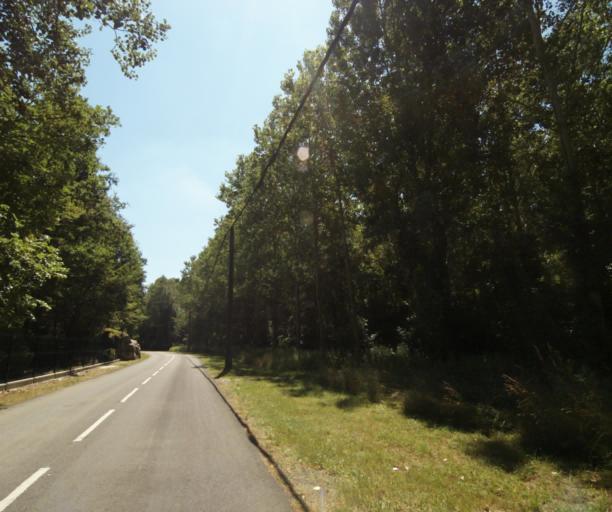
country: FR
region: Centre
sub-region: Departement du Loiret
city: Malesherbes
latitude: 48.2976
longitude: 2.4247
